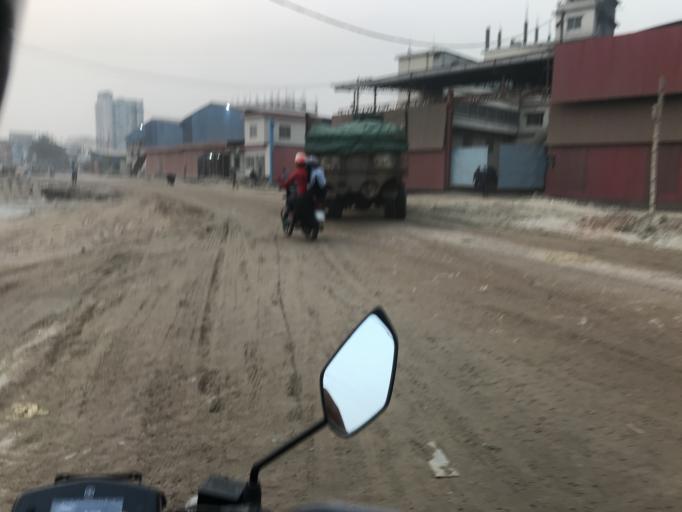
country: BD
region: Dhaka
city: Paltan
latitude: 23.7167
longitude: 90.4665
